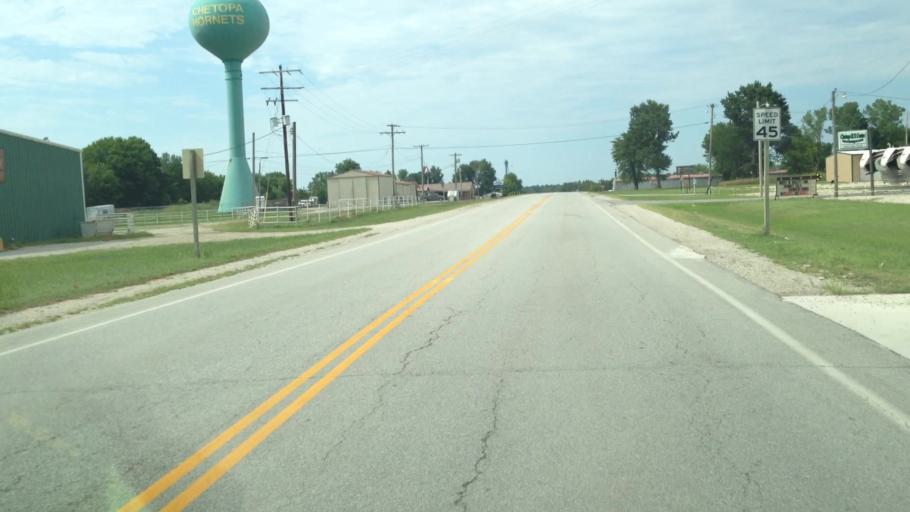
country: US
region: Kansas
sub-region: Labette County
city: Chetopa
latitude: 37.0407
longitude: -95.1002
